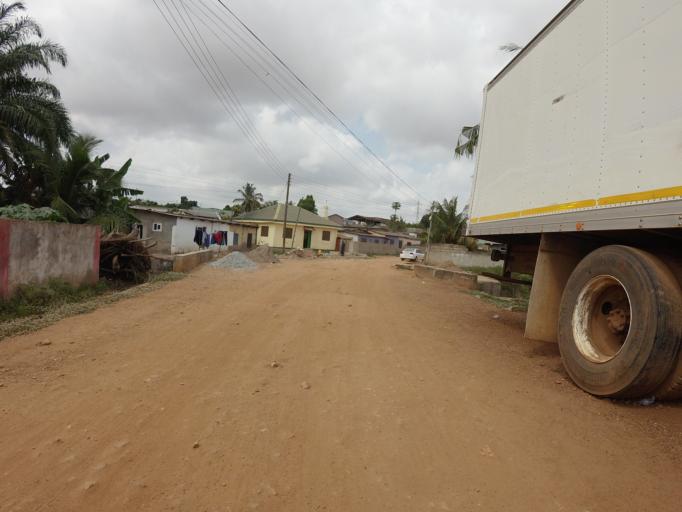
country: GH
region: Greater Accra
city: Dome
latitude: 5.6182
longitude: -0.2449
